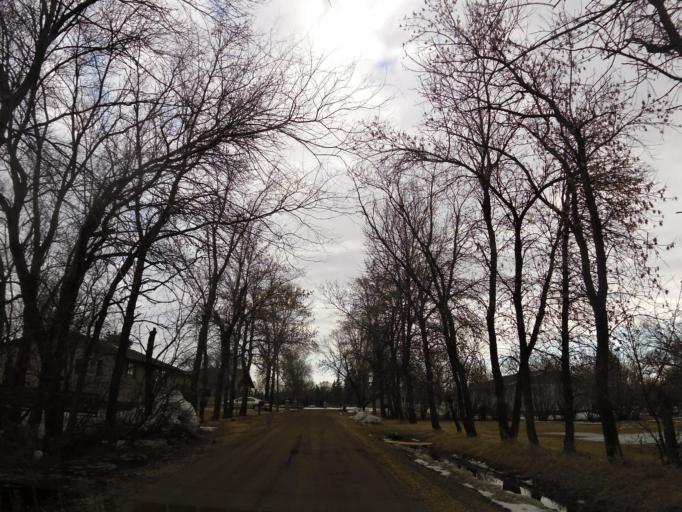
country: US
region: North Dakota
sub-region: Walsh County
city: Grafton
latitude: 48.4202
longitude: -97.4354
